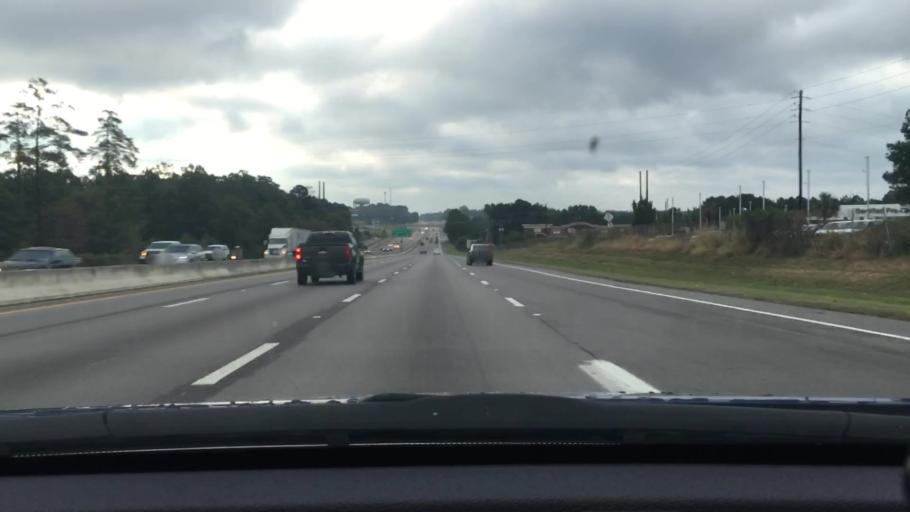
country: US
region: South Carolina
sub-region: Lexington County
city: Seven Oaks
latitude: 34.0752
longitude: -81.1501
